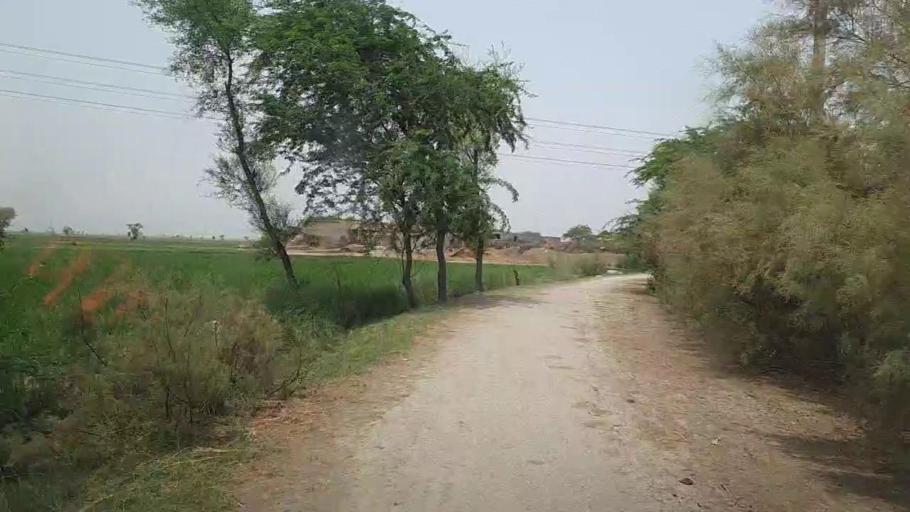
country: PK
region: Sindh
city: Sita Road
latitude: 27.0671
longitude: 67.8473
